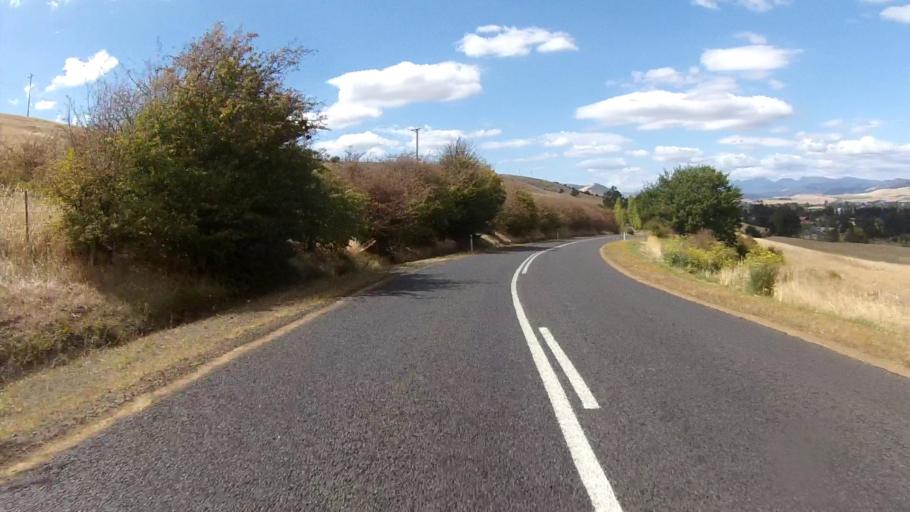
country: AU
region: Tasmania
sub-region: Derwent Valley
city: New Norfolk
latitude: -42.6908
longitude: 146.8822
